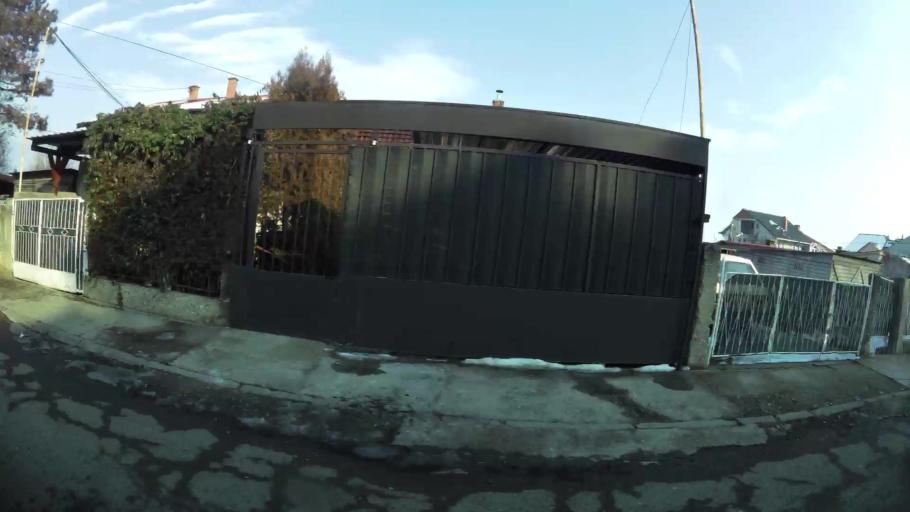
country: MK
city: Creshevo
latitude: 42.0145
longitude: 21.5086
